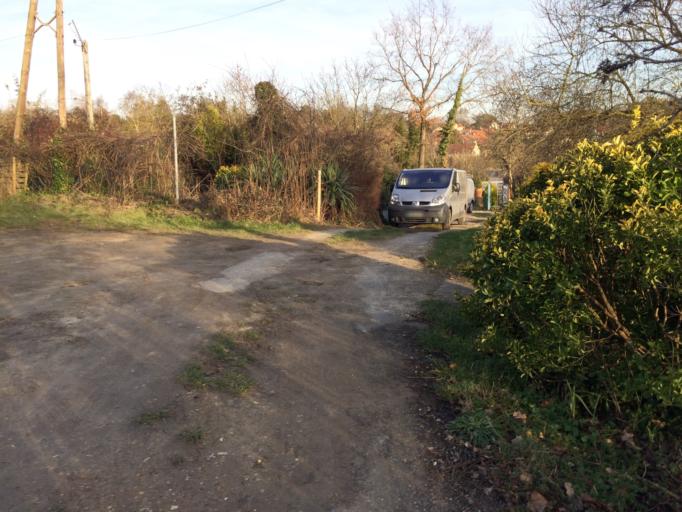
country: FR
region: Ile-de-France
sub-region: Departement de l'Essonne
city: Champlan
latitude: 48.7084
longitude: 2.2671
